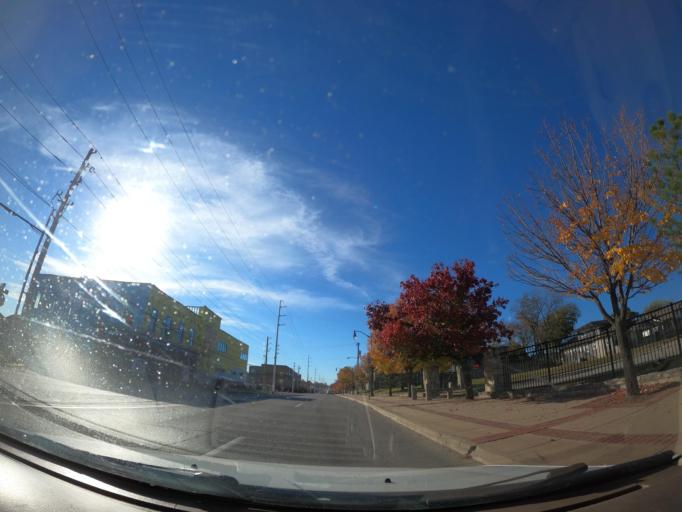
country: US
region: Oklahoma
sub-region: Tulsa County
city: Tulsa
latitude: 36.1539
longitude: -95.9584
